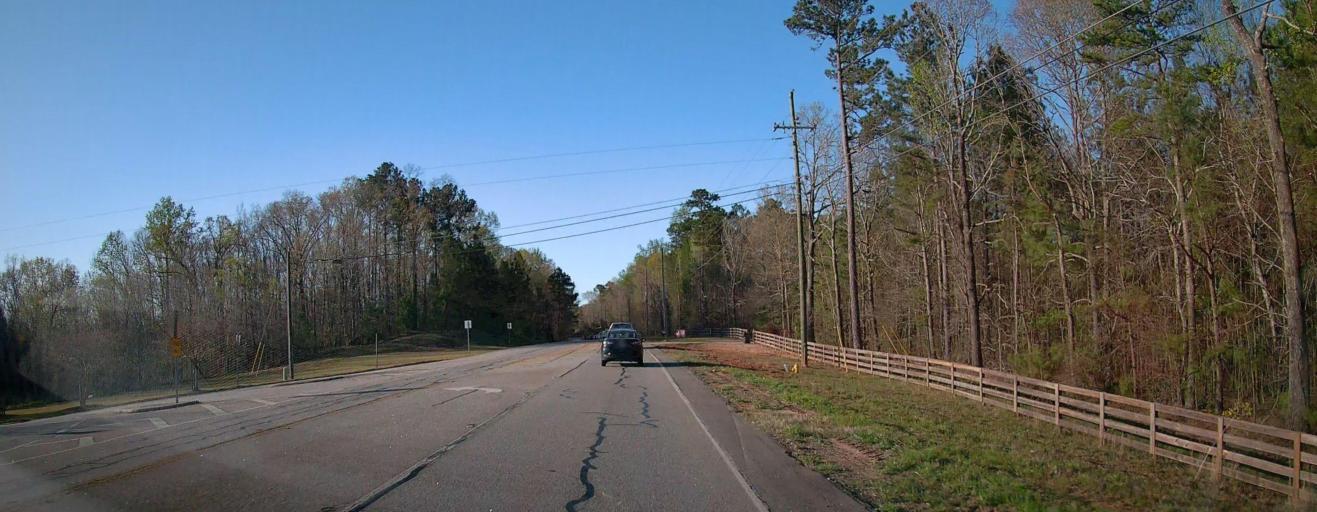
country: US
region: Georgia
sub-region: Newton County
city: Oakwood
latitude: 33.4312
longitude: -83.8960
